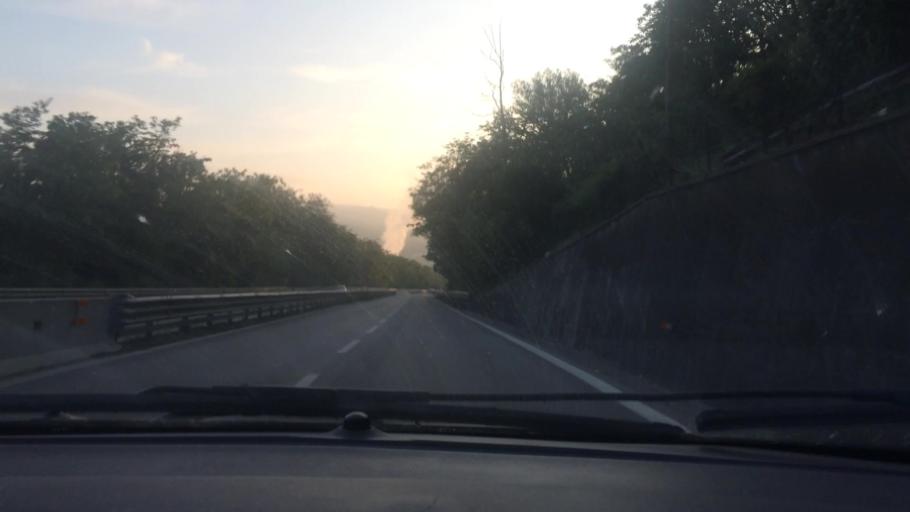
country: IT
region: Basilicate
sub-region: Provincia di Potenza
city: Potenza
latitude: 40.6315
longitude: 15.8222
